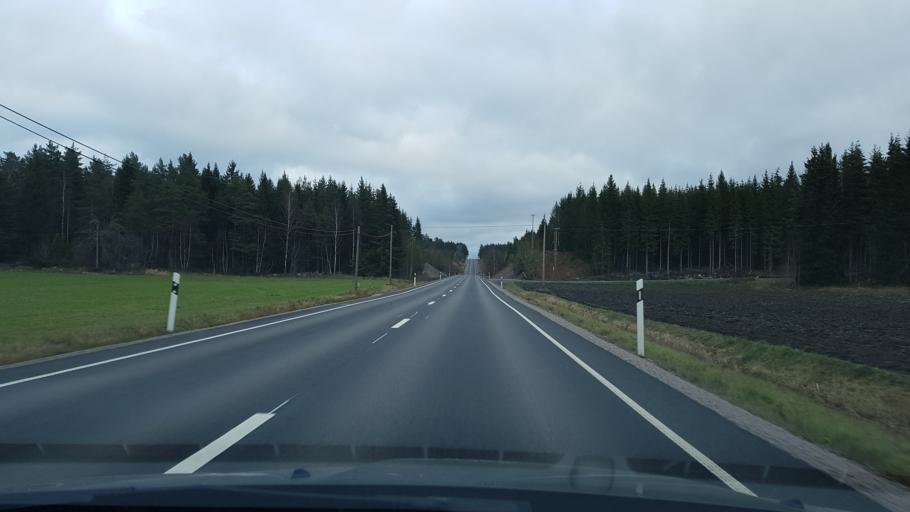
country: SE
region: Stockholm
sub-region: Norrtalje Kommun
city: Nykvarn
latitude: 59.9925
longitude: 18.2773
